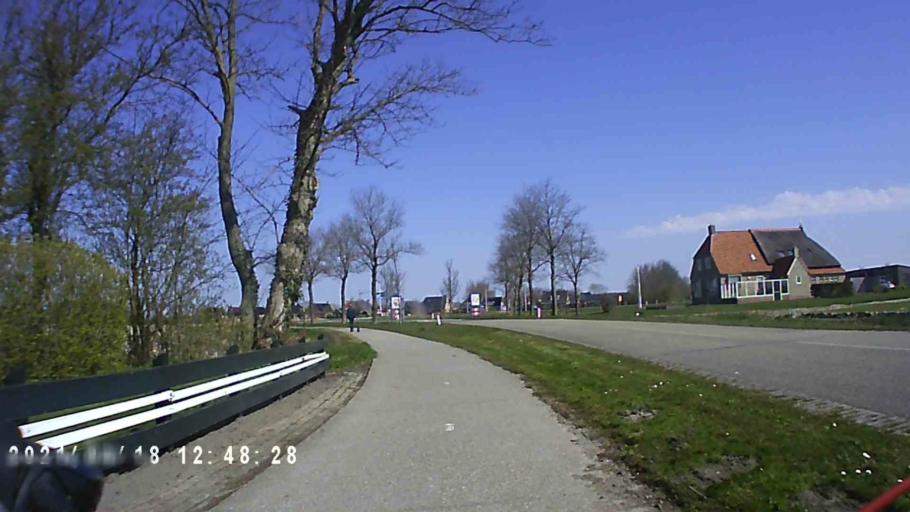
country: NL
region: Friesland
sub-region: Gemeente Dongeradeel
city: Dokkum
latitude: 53.3733
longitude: 6.0513
